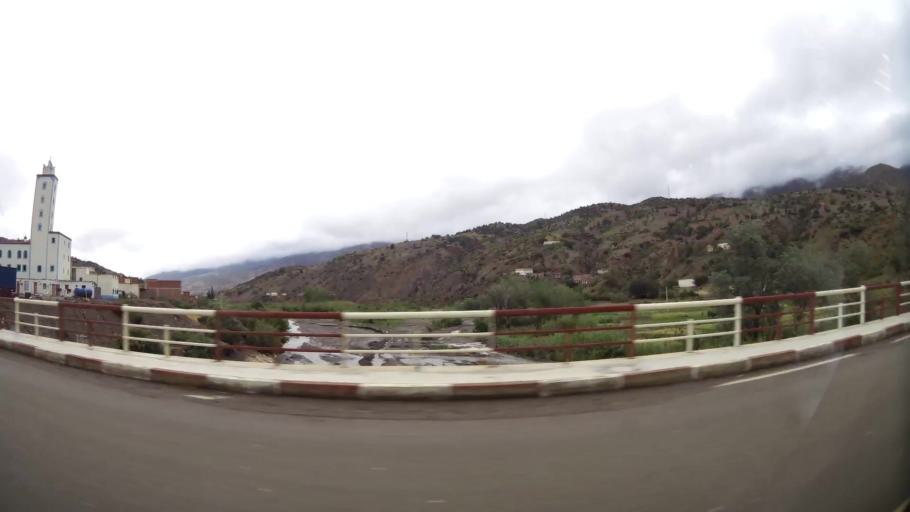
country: MA
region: Taza-Al Hoceima-Taounate
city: Imzourene
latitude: 34.9647
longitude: -3.8133
